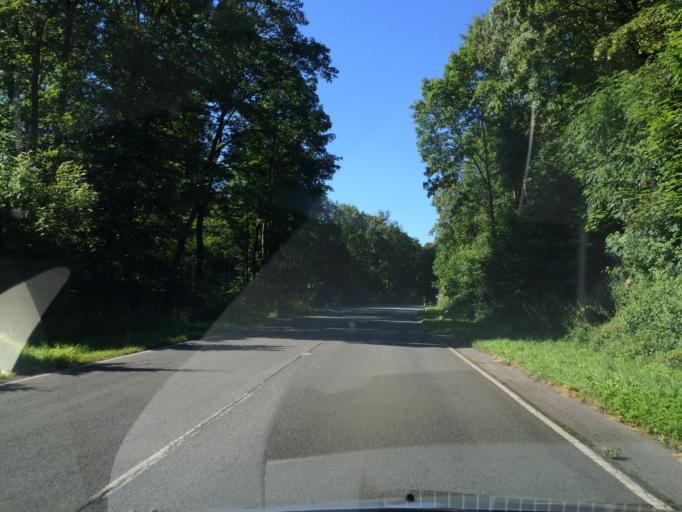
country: DE
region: North Rhine-Westphalia
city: Iserlohn
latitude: 51.3588
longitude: 7.7007
